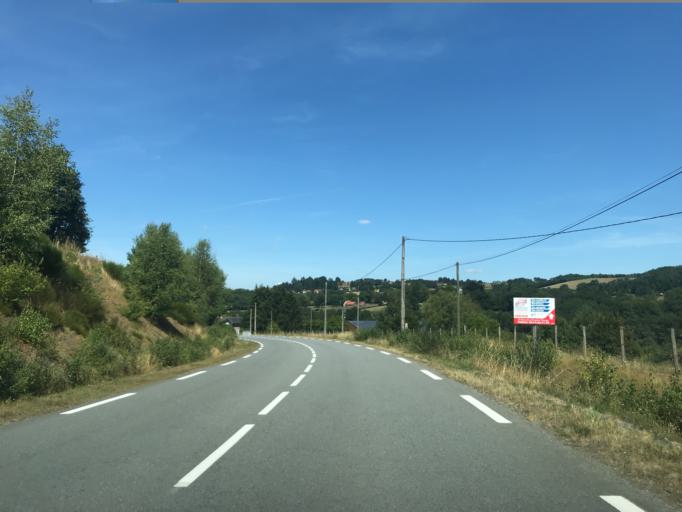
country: FR
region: Limousin
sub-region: Departement de la Creuse
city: Felletin
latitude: 45.8650
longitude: 2.1696
